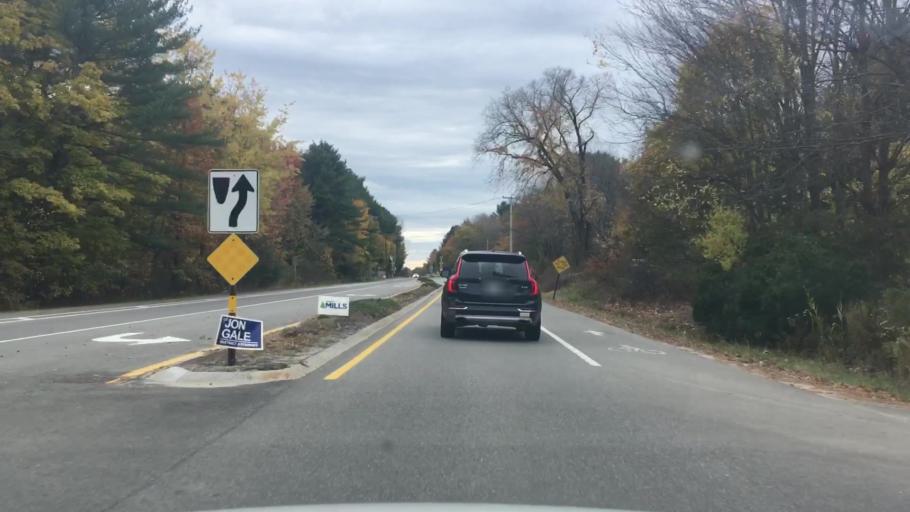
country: US
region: Maine
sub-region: Cumberland County
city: Falmouth
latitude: 43.7066
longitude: -70.2366
